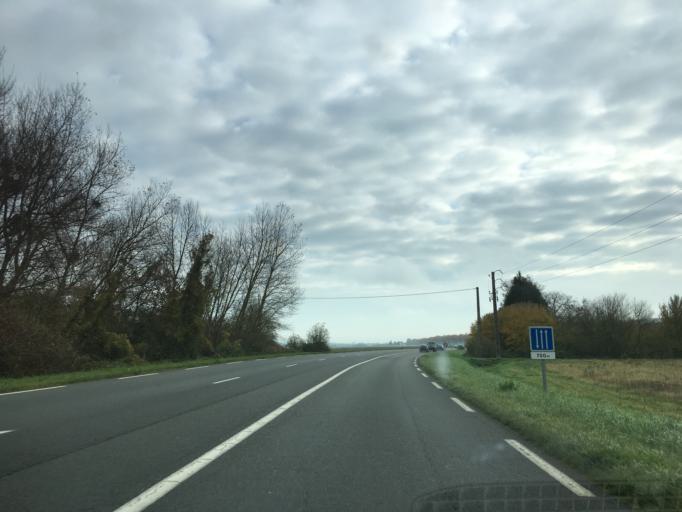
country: FR
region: Bourgogne
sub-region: Departement de l'Yonne
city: Champigny
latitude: 48.3140
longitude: 3.1546
